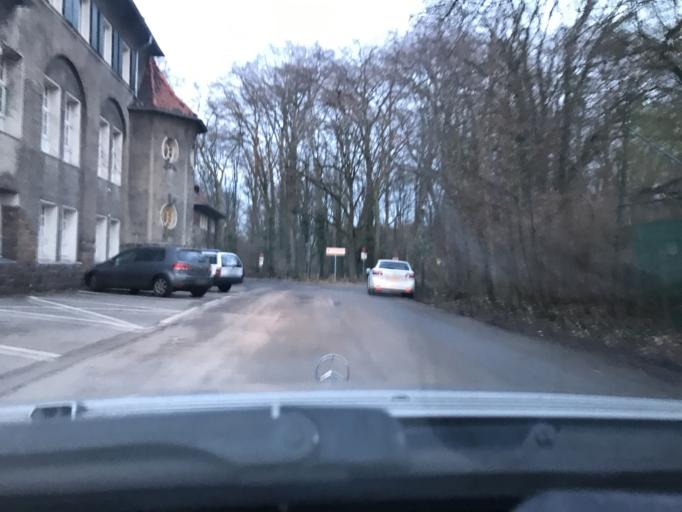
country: DE
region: North Rhine-Westphalia
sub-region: Regierungsbezirk Dusseldorf
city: Krefeld
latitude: 51.3516
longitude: 6.5861
